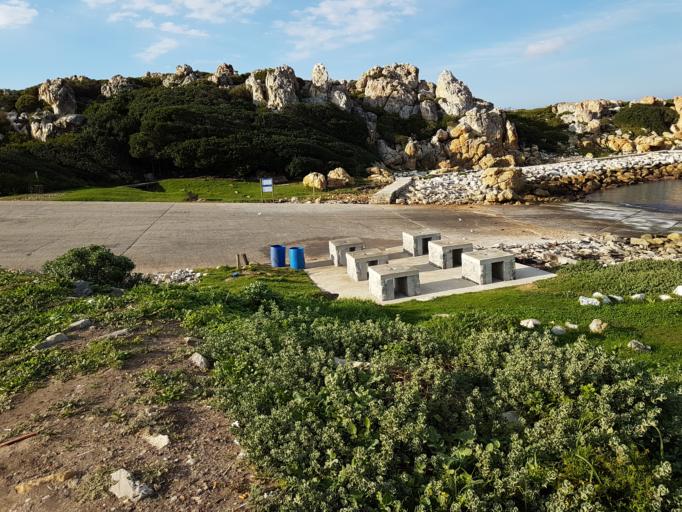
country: ZA
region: Western Cape
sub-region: Overberg District Municipality
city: Grabouw
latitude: -34.3454
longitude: 19.0134
